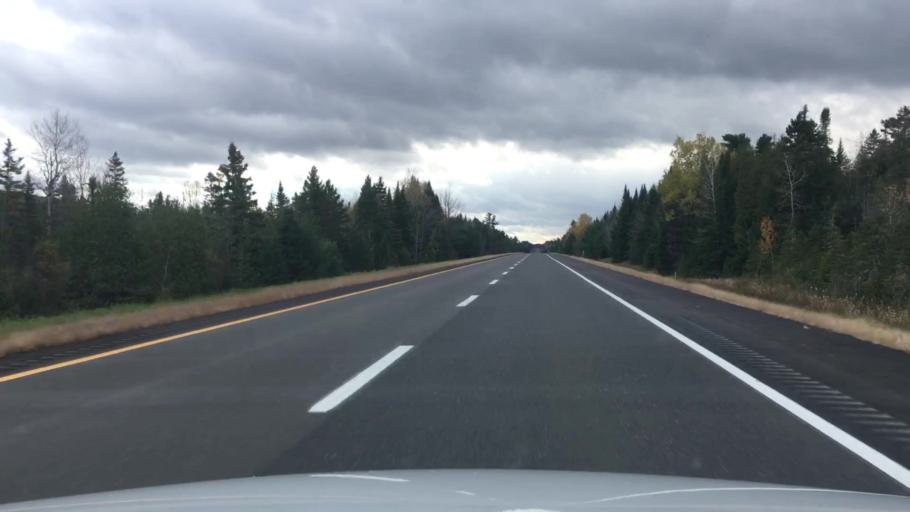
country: US
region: Maine
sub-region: Penobscot County
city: Patten
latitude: 46.0803
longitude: -68.2144
